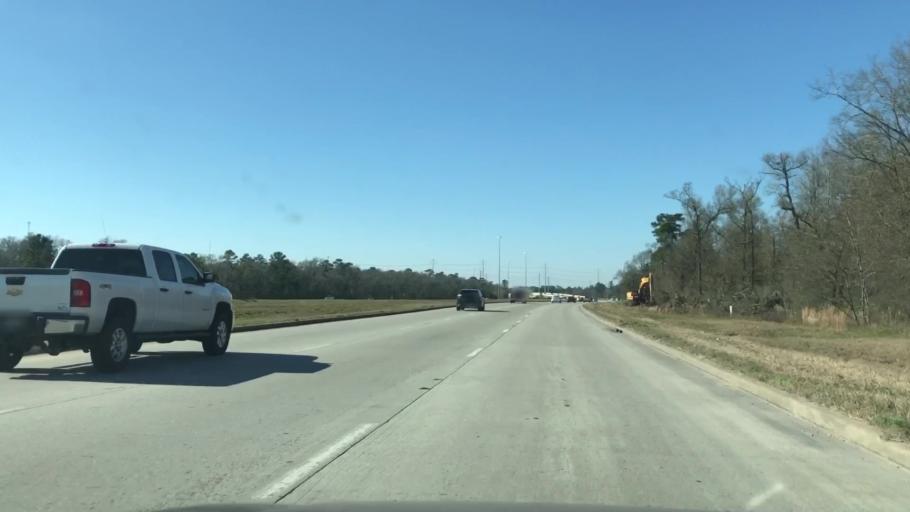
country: US
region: Texas
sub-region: Harris County
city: Cloverleaf
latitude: 29.8244
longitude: -95.1958
